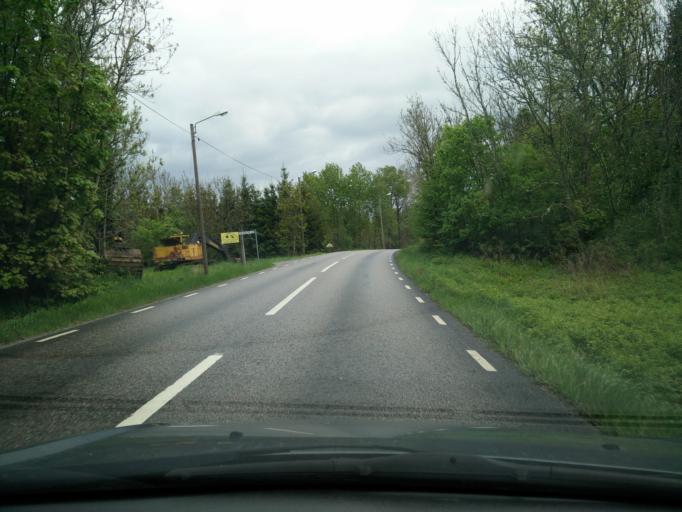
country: SE
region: Stockholm
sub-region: Norrtalje Kommun
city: Bjorko
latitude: 59.8176
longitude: 18.8947
